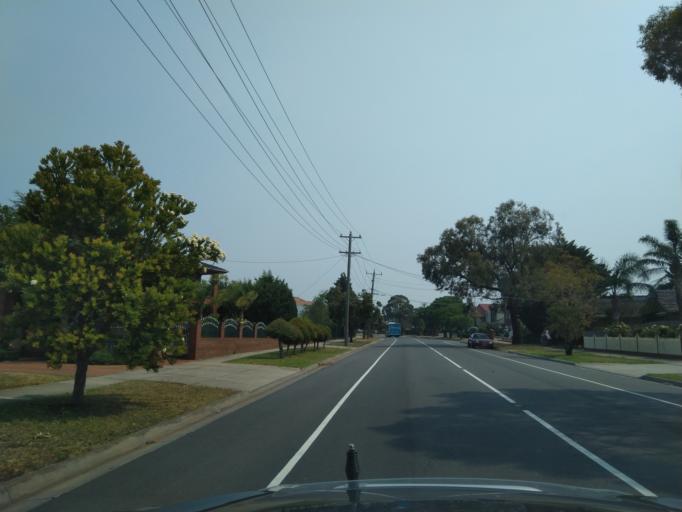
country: AU
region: Victoria
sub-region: Hume
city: Meadow Heights
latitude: -37.6452
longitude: 144.8981
